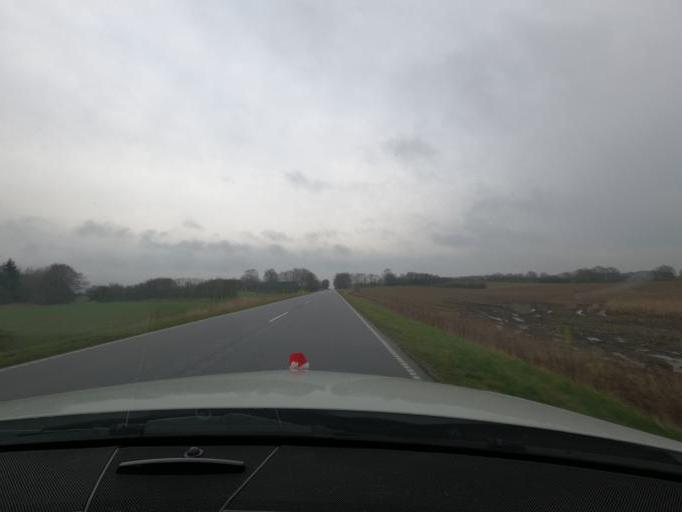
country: DK
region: South Denmark
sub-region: Haderslev Kommune
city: Vojens
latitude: 55.1756
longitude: 9.3905
